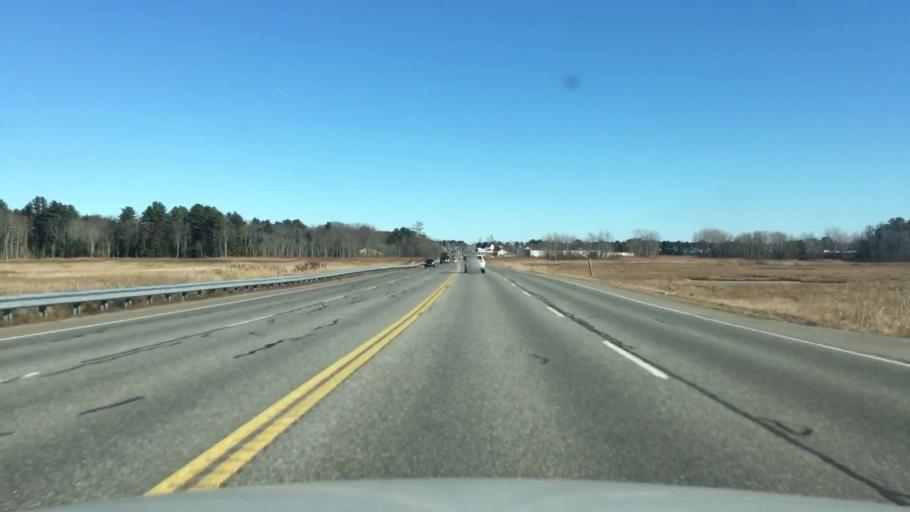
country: US
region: Maine
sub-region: Cumberland County
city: West Scarborough
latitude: 43.5783
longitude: -70.3733
